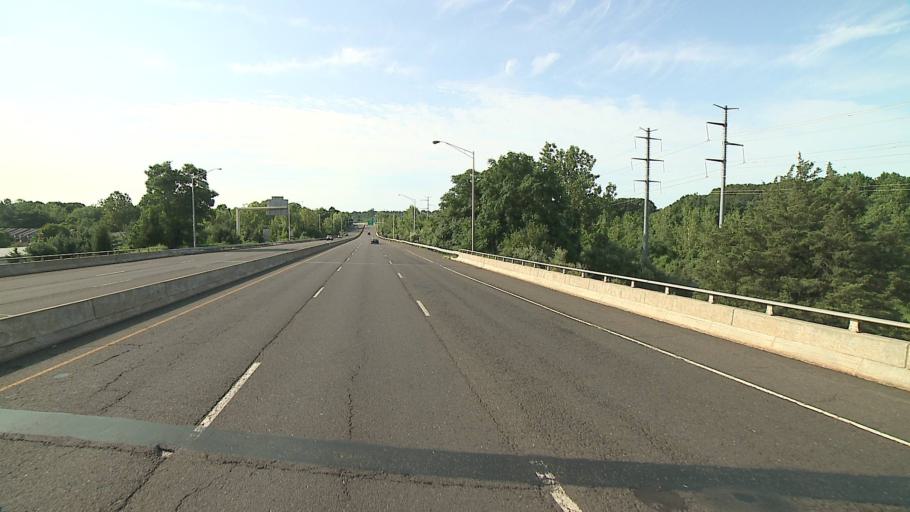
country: US
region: Connecticut
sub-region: Fairfield County
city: Norwalk
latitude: 41.1369
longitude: -73.4300
